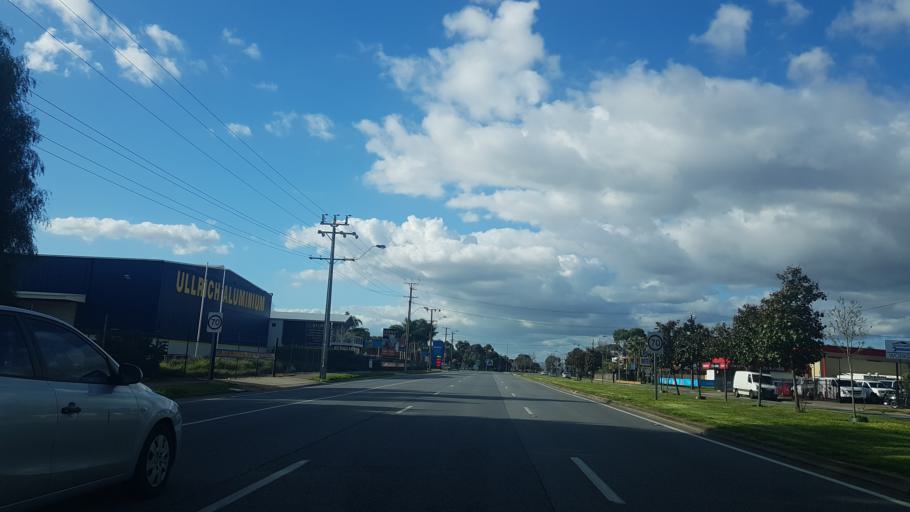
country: AU
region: South Australia
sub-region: Salisbury
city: Ingle Farm
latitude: -34.8283
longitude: 138.6144
